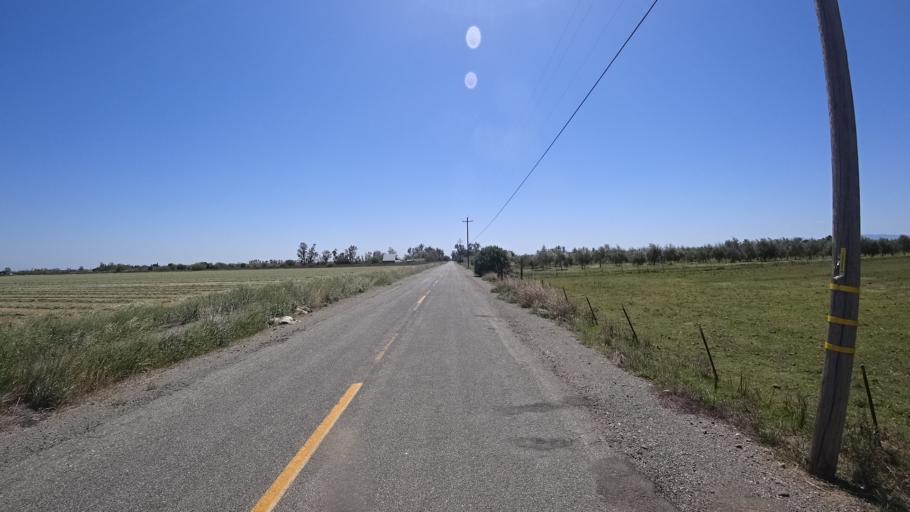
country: US
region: California
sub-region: Glenn County
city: Orland
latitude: 39.7767
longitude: -122.1782
